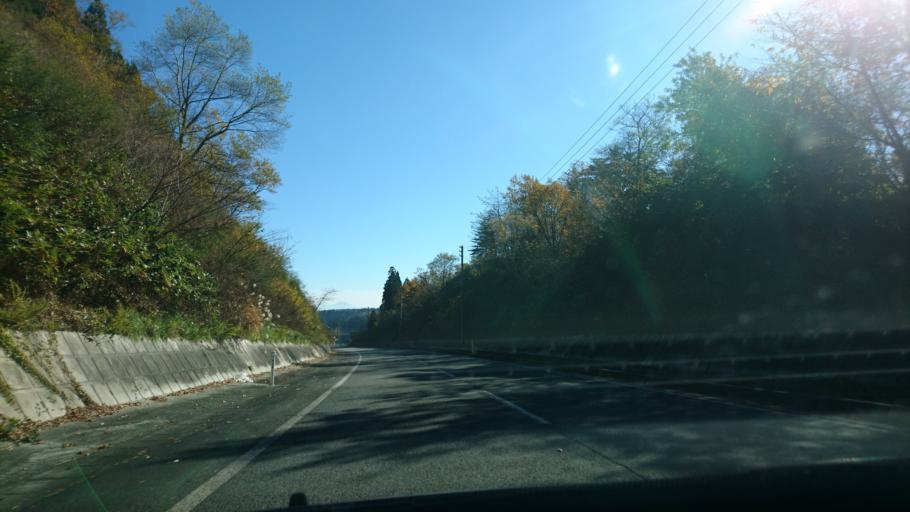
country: JP
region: Iwate
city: Mizusawa
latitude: 39.1212
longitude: 140.9406
